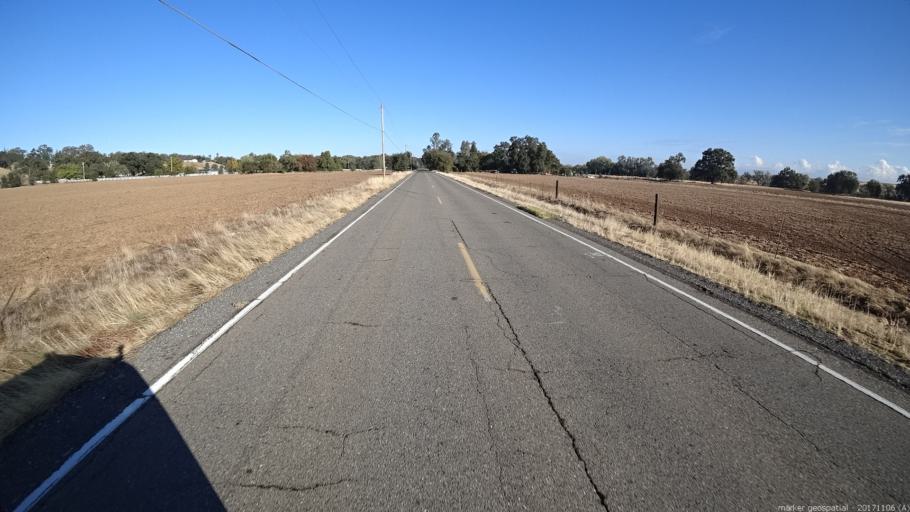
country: US
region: California
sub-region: Shasta County
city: Anderson
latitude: 40.4896
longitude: -122.2388
